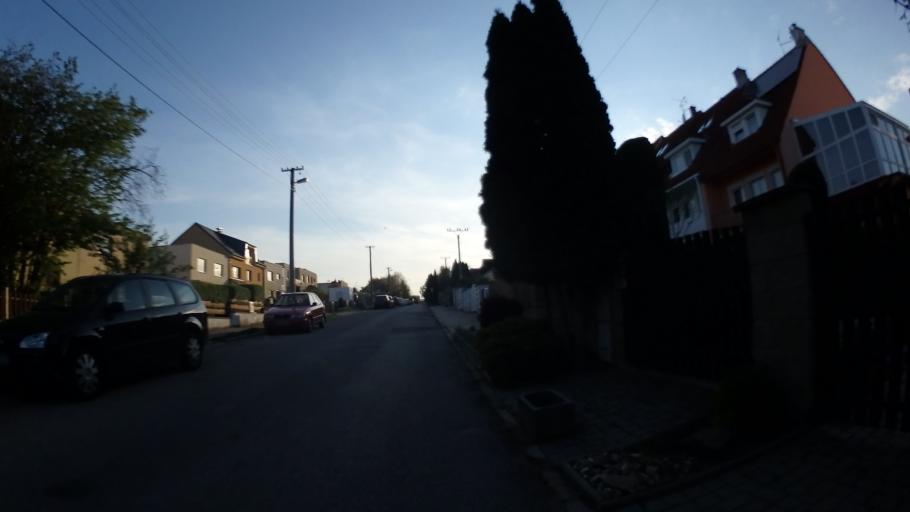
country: CZ
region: South Moravian
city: Moravany
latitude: 49.1492
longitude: 16.5746
